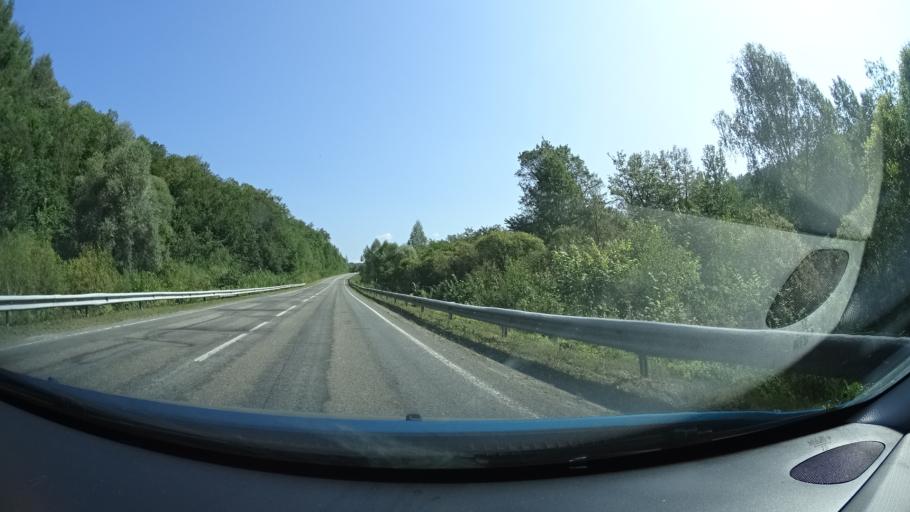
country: RU
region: Bashkortostan
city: Inzer
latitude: 54.3378
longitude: 57.0972
